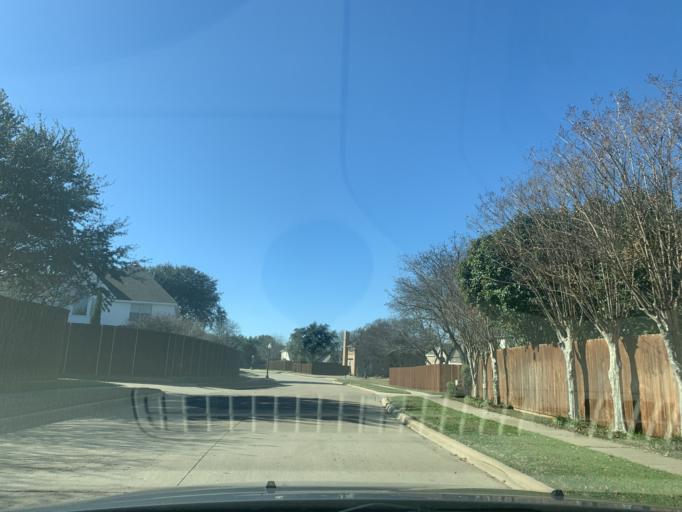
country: US
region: Texas
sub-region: Denton County
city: The Colony
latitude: 33.0603
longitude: -96.8339
